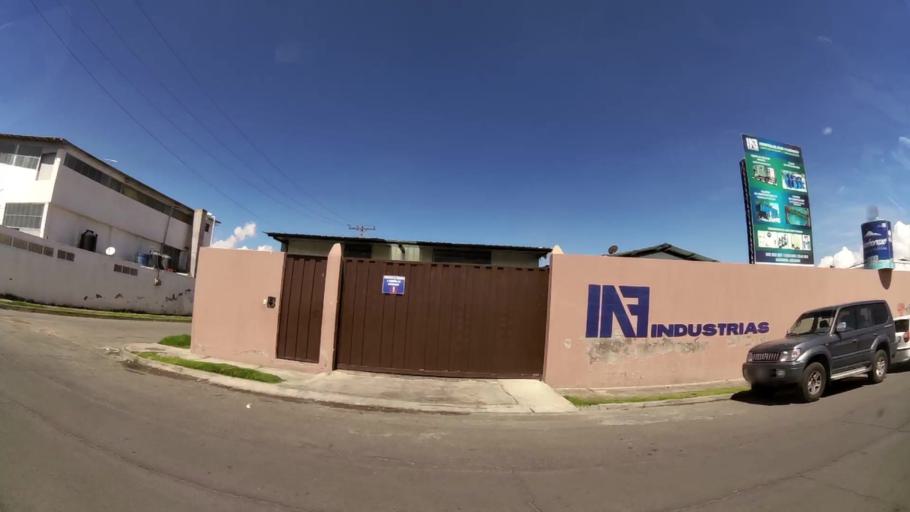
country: EC
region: Chimborazo
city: Riobamba
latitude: -1.6768
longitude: -78.6319
